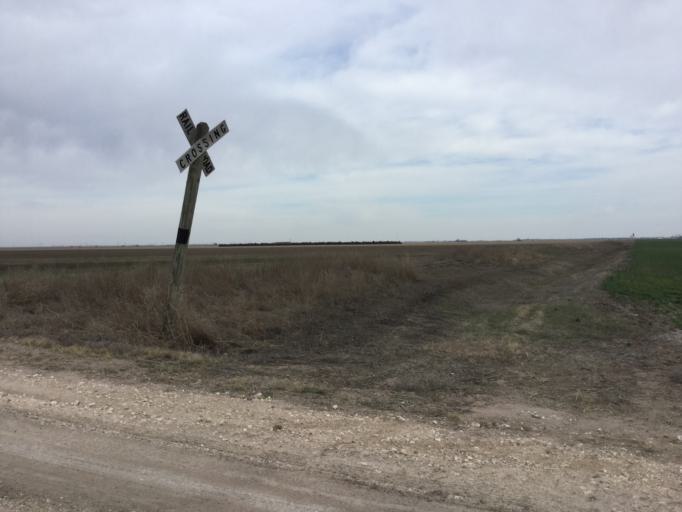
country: US
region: Kansas
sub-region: Scott County
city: Scott City
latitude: 38.4100
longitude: -100.9153
